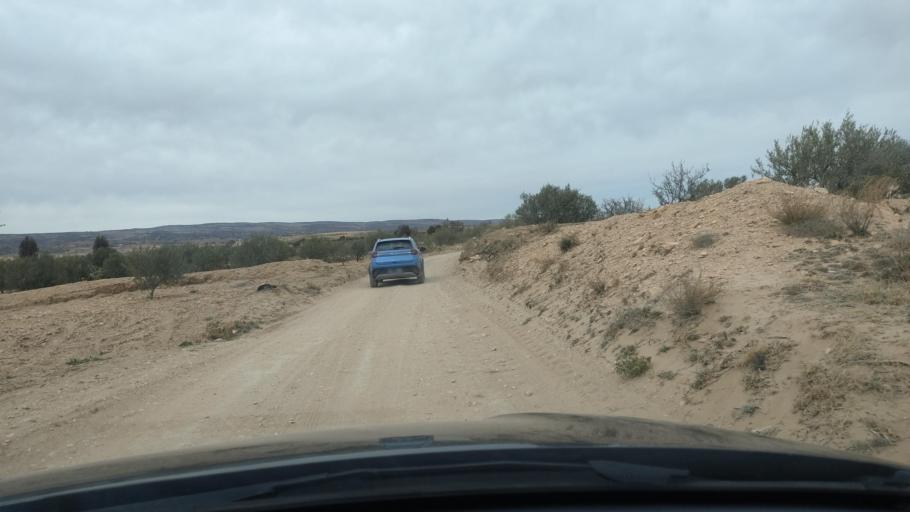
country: TN
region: Al Qasrayn
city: Kasserine
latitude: 35.2542
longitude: 8.9217
